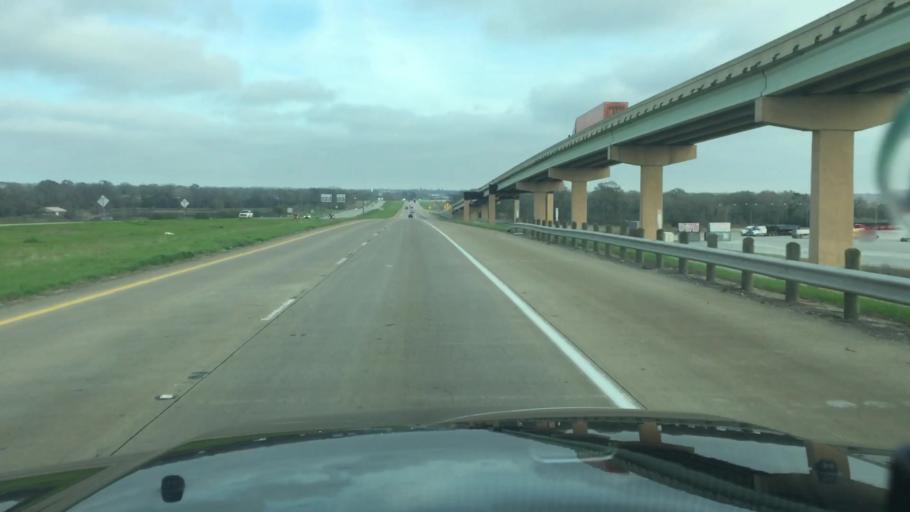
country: US
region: Texas
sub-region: Waller County
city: Hempstead
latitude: 30.1147
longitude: -96.0721
